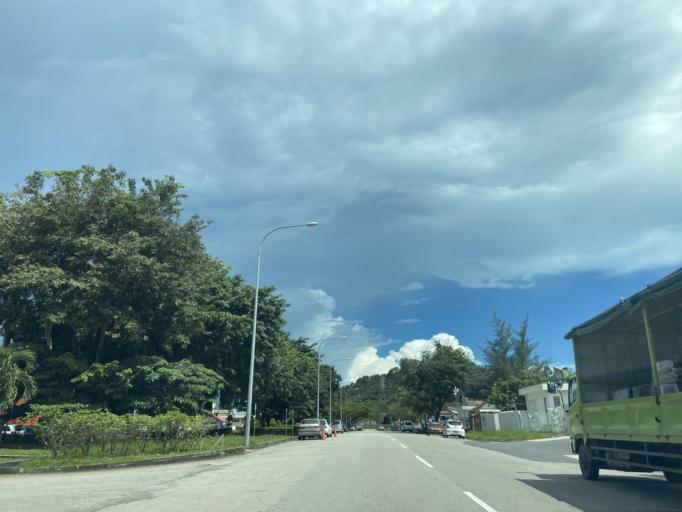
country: SG
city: Singapore
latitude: 1.0558
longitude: 104.0383
